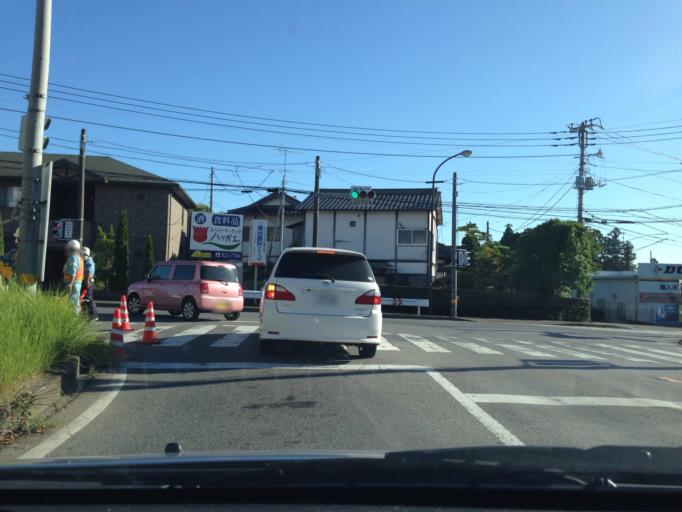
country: JP
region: Ibaraki
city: Naka
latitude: 36.0653
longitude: 140.1897
